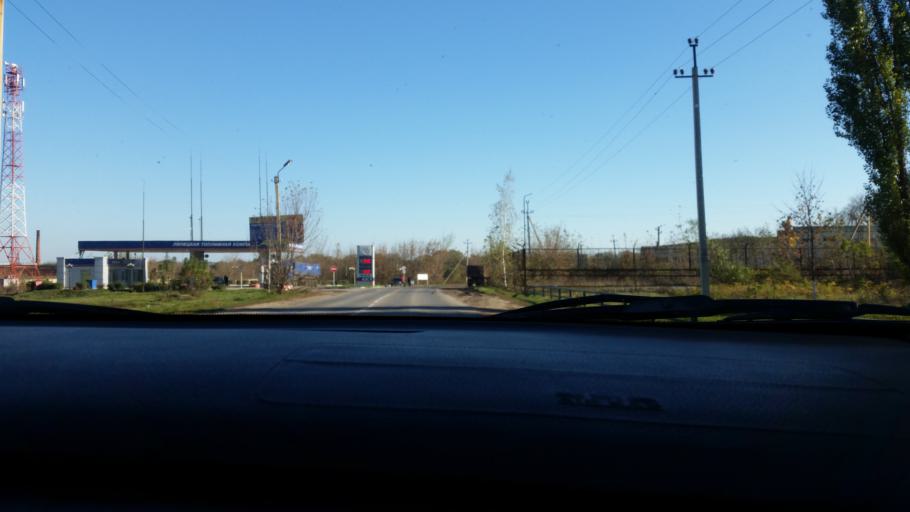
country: RU
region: Lipetsk
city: Gryazi
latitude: 52.4733
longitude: 39.9571
